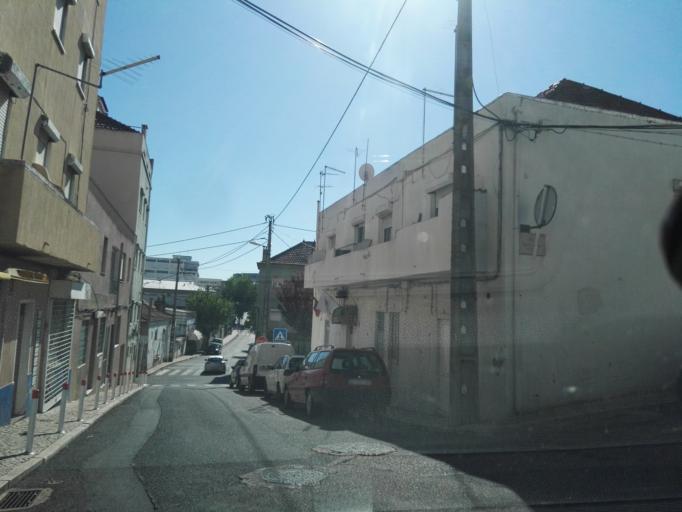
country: PT
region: Lisbon
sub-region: Loures
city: Sacavem
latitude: 38.7904
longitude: -9.1202
